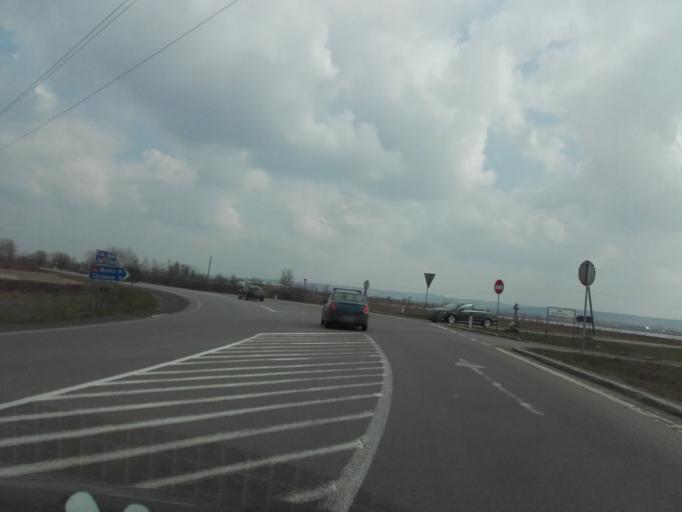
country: RO
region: Mures
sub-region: Comuna Iernut
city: Iernut
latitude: 46.4450
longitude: 24.2509
